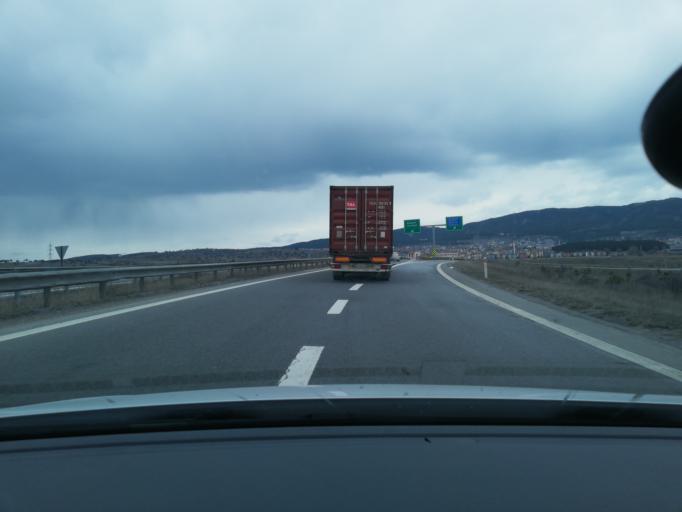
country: TR
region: Bolu
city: Gerede
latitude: 40.7772
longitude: 32.2119
